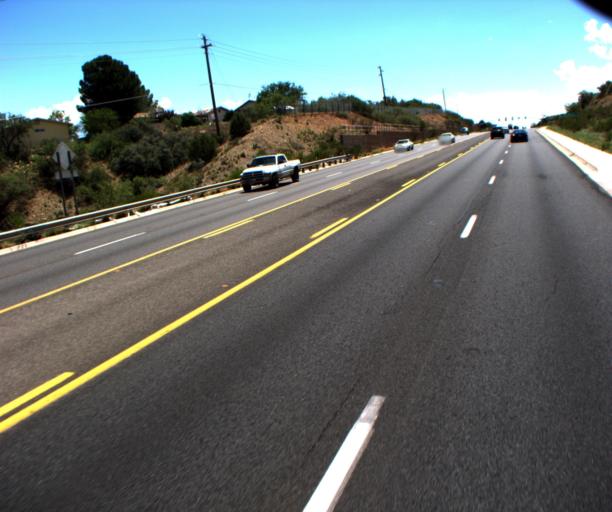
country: US
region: Arizona
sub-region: Yavapai County
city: Verde Village
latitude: 34.7020
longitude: -111.9892
